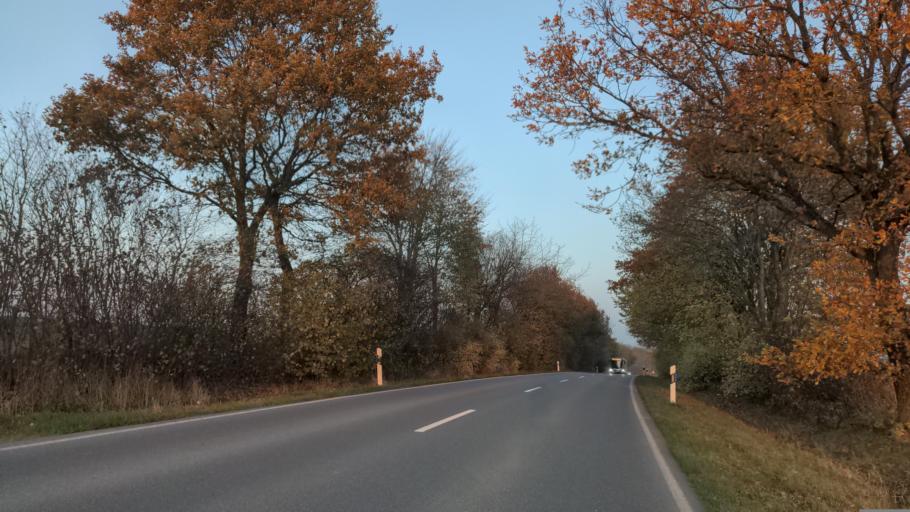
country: DE
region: Schleswig-Holstein
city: Malente
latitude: 54.1180
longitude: 10.5578
